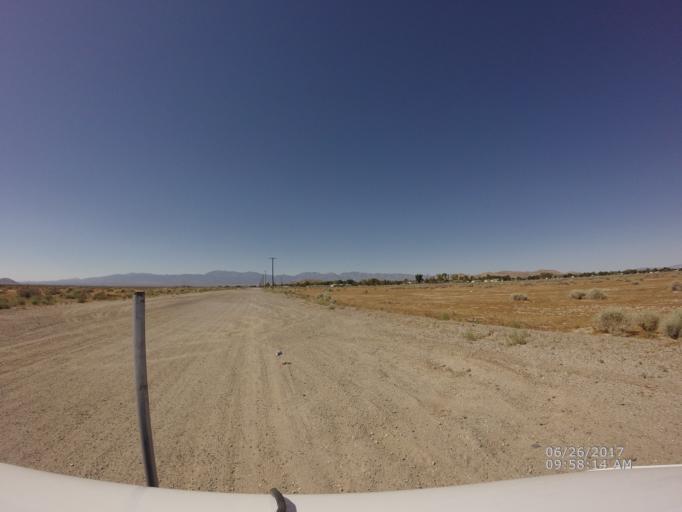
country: US
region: California
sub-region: Los Angeles County
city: Lake Los Angeles
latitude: 34.6336
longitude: -117.8094
